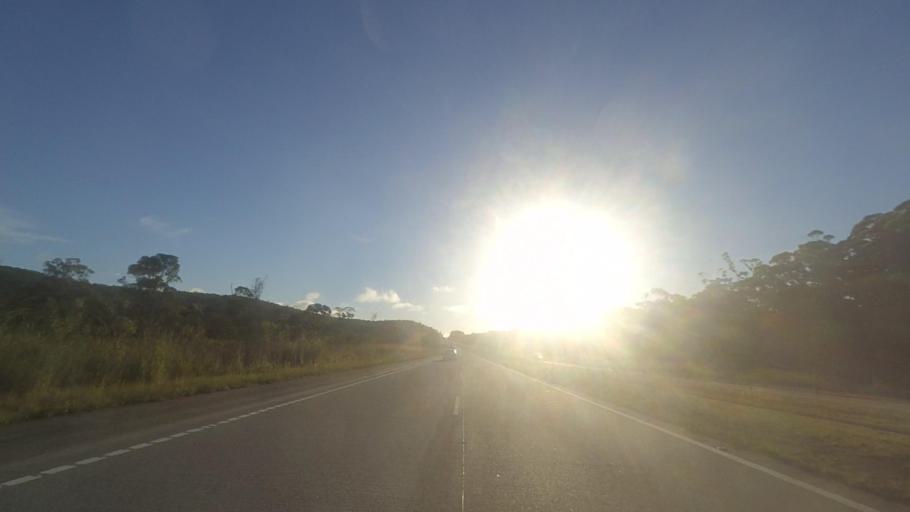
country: AU
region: New South Wales
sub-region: Great Lakes
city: Bulahdelah
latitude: -32.5286
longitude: 152.1893
